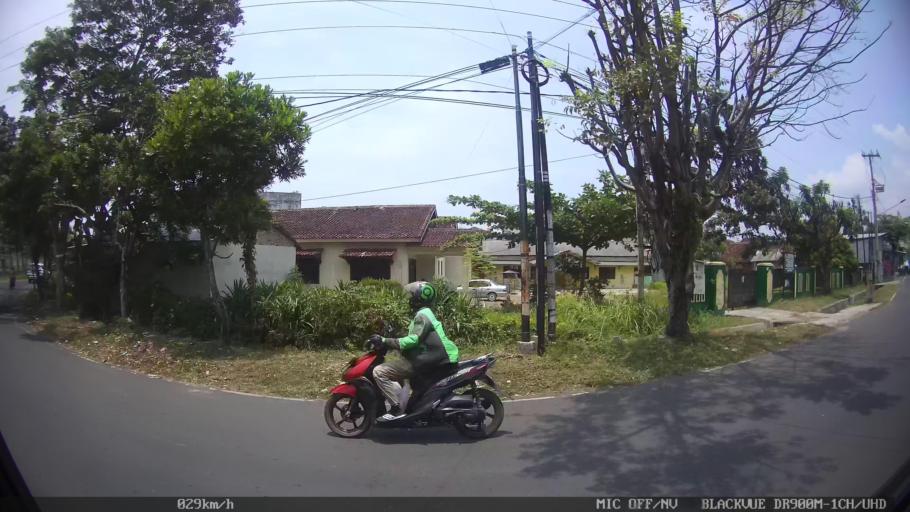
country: ID
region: Lampung
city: Bandarlampung
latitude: -5.4434
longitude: 105.2705
